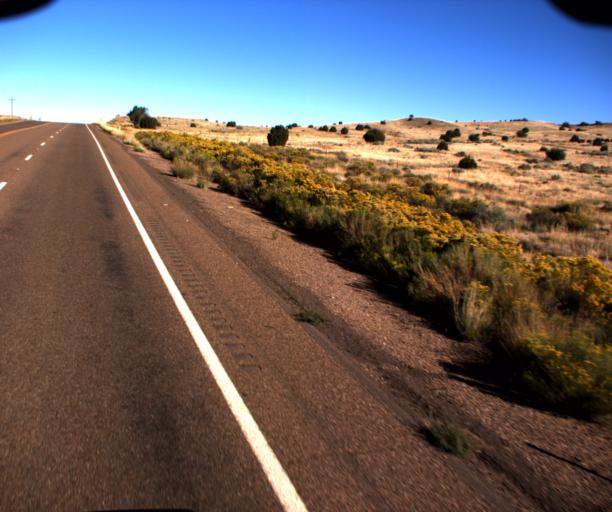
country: US
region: Arizona
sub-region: Navajo County
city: Taylor
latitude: 34.4279
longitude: -110.0906
